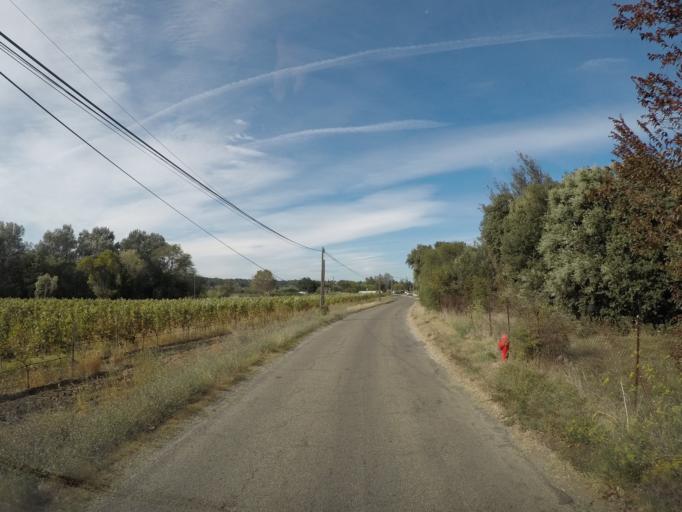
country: FR
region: Provence-Alpes-Cote d'Azur
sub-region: Departement du Vaucluse
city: Bollene
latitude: 44.2839
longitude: 4.7690
